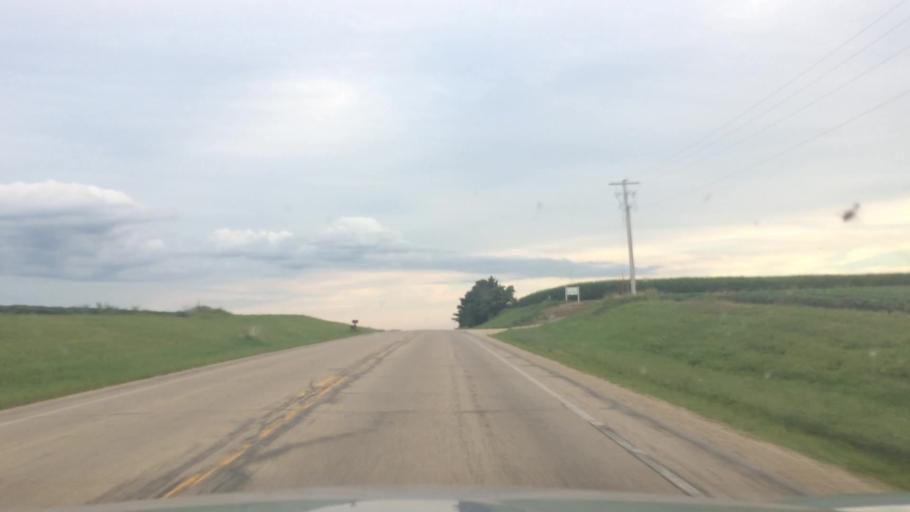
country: US
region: Wisconsin
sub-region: Columbia County
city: Lodi
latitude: 43.2440
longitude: -89.5211
